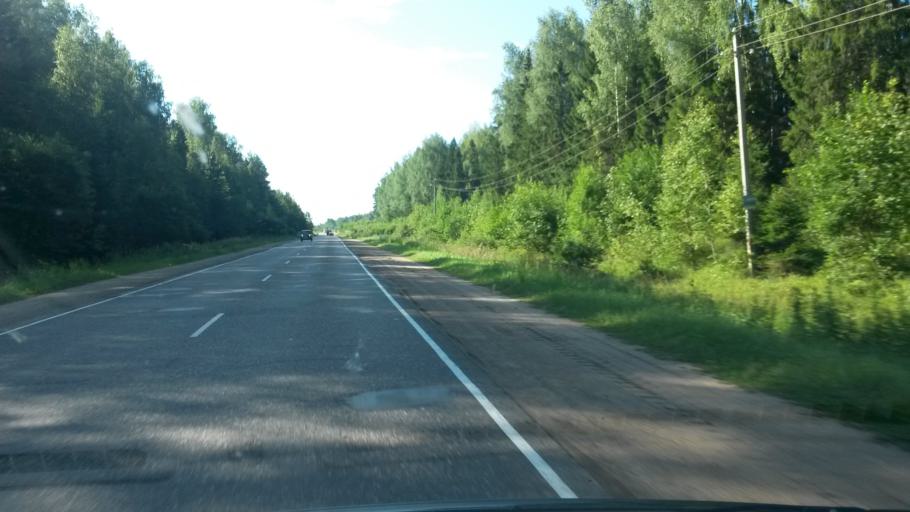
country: RU
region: Ivanovo
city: Novo-Talitsy
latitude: 57.0466
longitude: 40.7388
